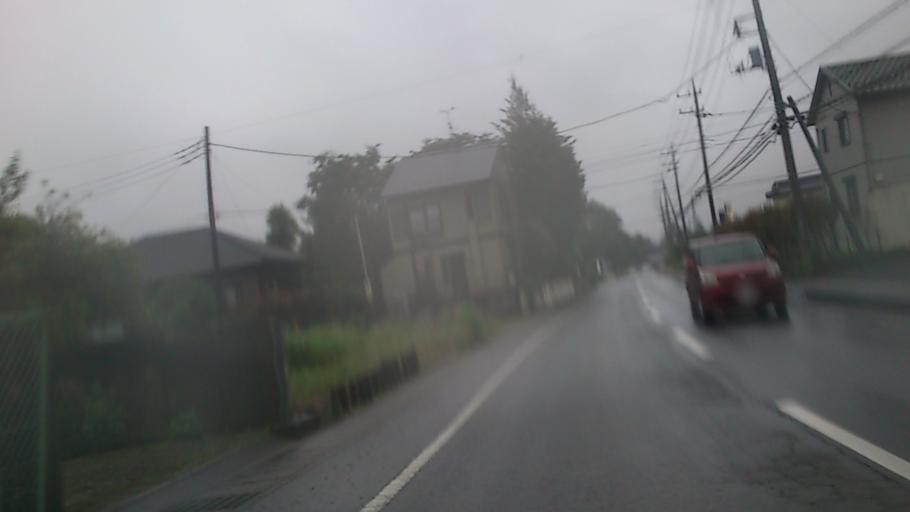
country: JP
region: Tochigi
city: Otawara
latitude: 36.9116
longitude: 139.9809
